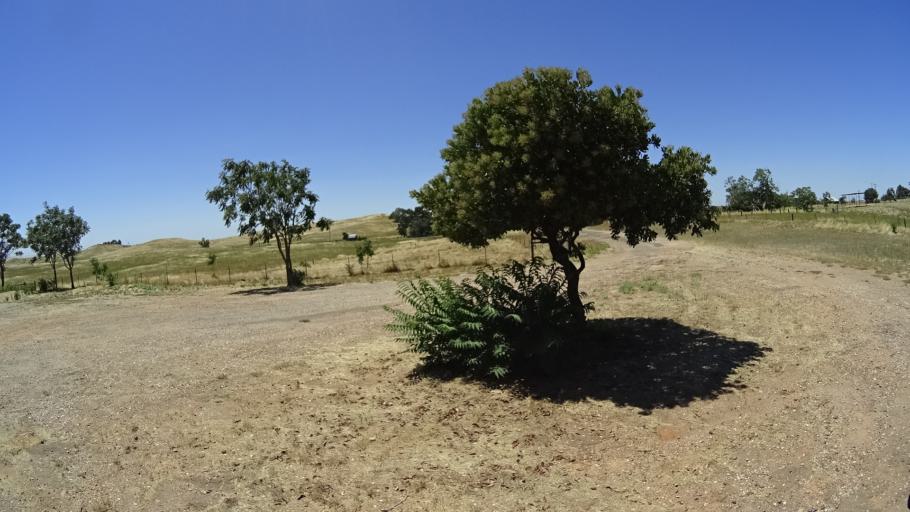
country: US
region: California
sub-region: Calaveras County
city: Rancho Calaveras
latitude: 38.0308
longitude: -120.8498
